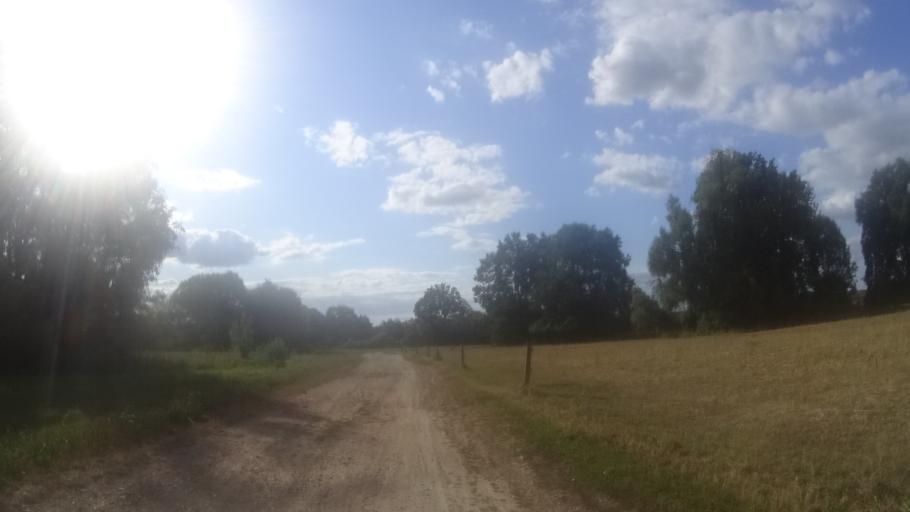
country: CZ
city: Albrechtice nad Orlici
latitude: 50.1643
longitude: 16.0361
